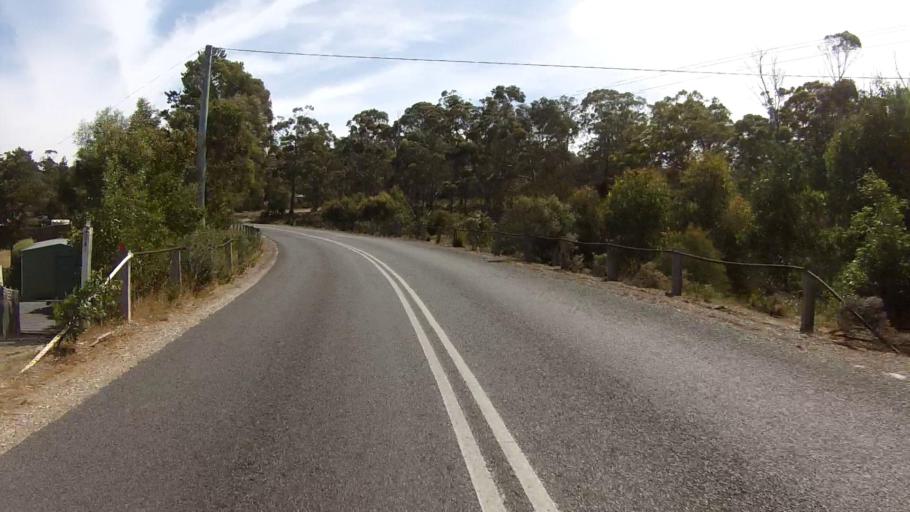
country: AU
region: Tasmania
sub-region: Huon Valley
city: Cygnet
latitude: -43.2702
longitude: 147.1476
